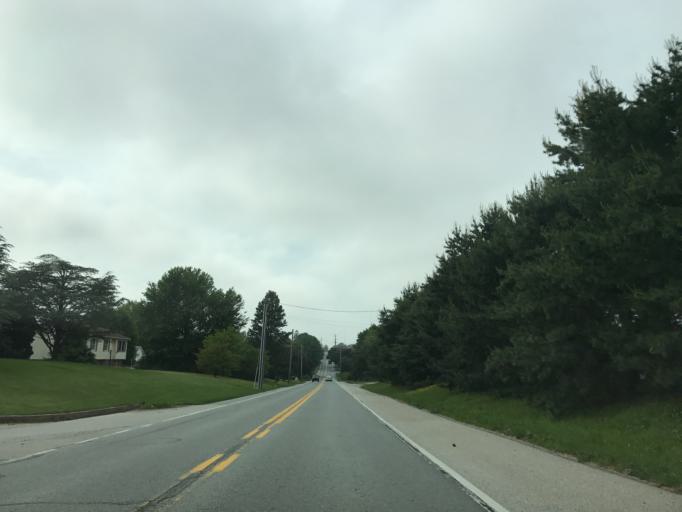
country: US
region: Pennsylvania
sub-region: York County
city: Windsor
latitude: 39.8919
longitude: -76.5581
